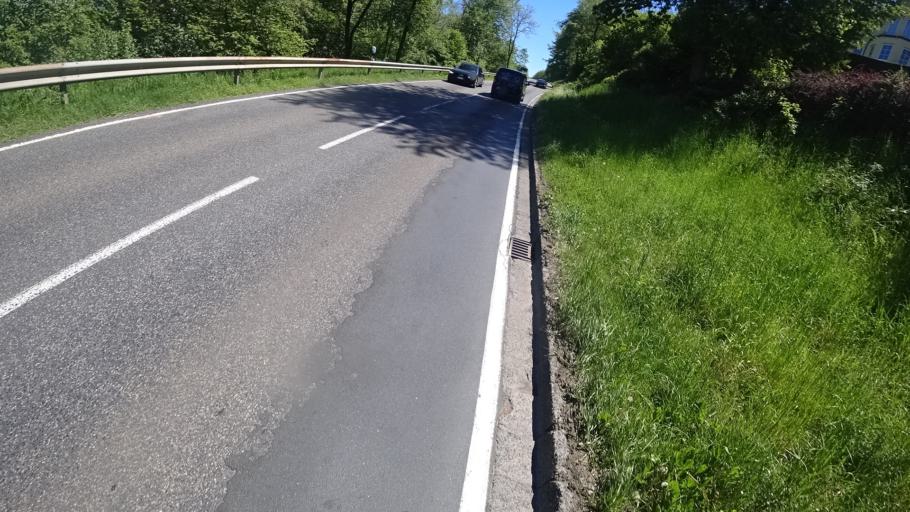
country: DE
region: Rheinland-Pfalz
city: Steineroth
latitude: 50.7580
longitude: 7.8554
